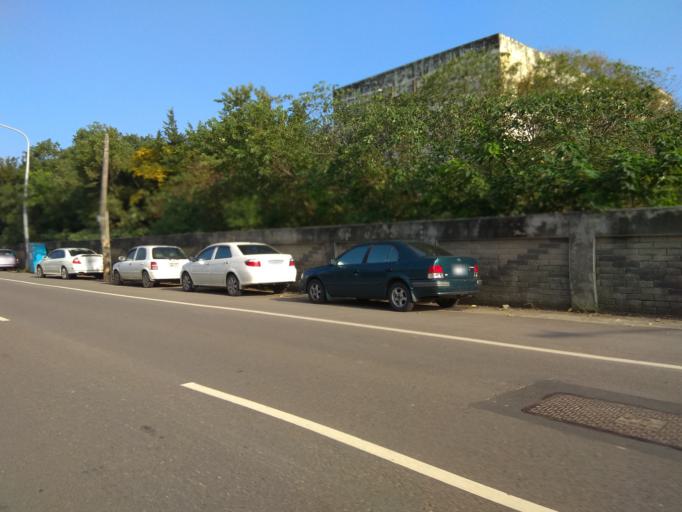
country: TW
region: Taiwan
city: Taoyuan City
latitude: 24.9675
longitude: 121.1398
